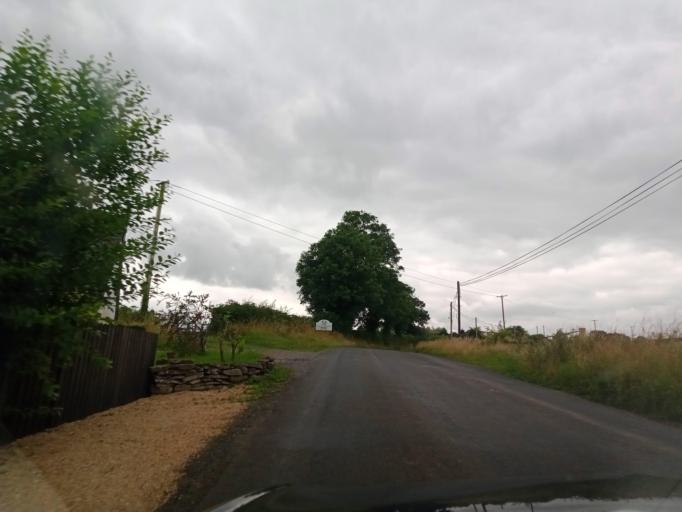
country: IE
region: Leinster
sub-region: Kilkenny
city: Castlecomer
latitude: 52.8938
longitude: -7.1516
